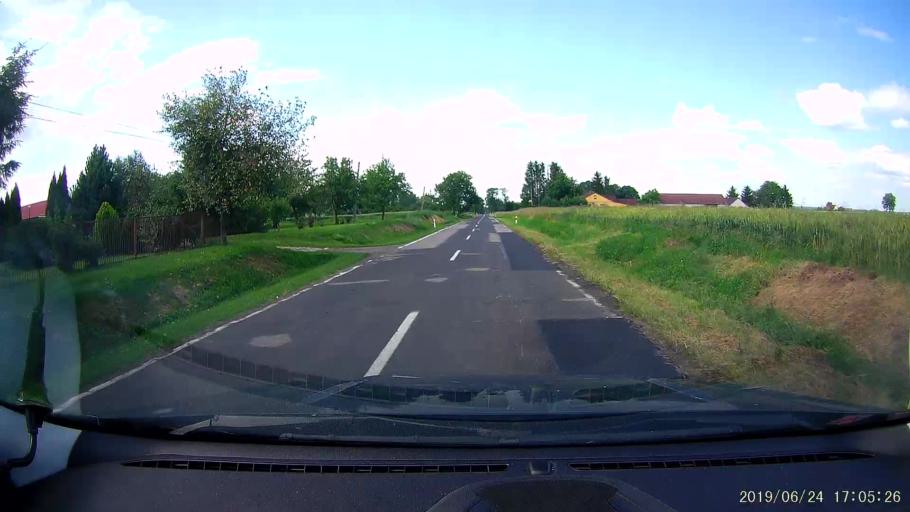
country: PL
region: Lublin Voivodeship
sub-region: Powiat hrubieszowski
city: Dolhobyczow
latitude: 50.5750
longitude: 23.9646
